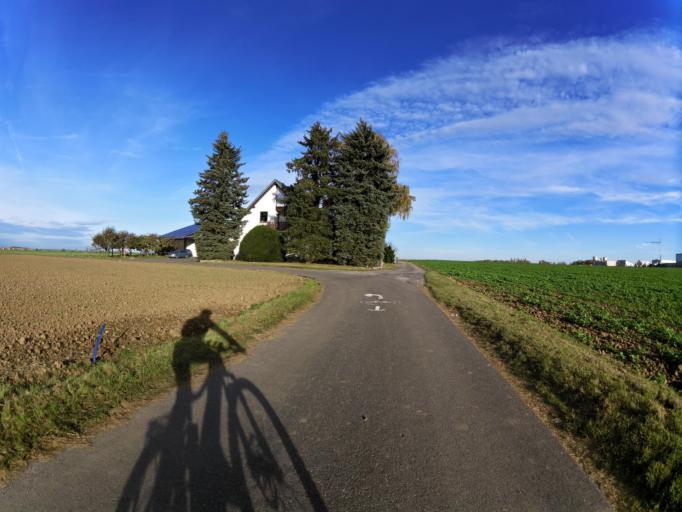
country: DE
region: Bavaria
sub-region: Regierungsbezirk Unterfranken
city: Giebelstadt
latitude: 49.6578
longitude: 9.9531
